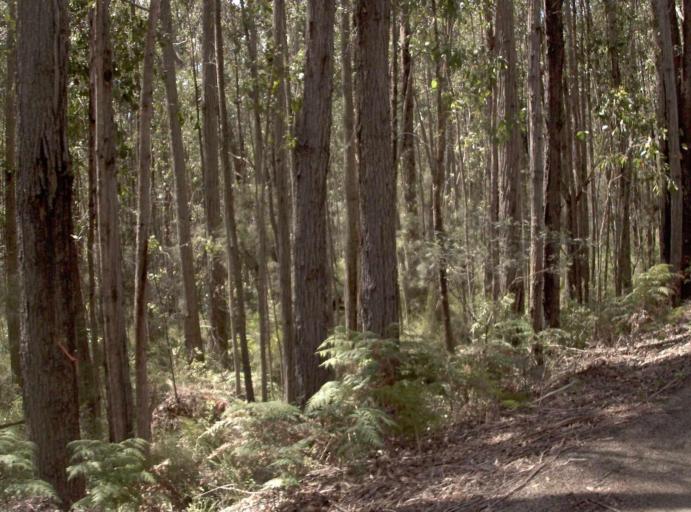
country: AU
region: New South Wales
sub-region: Bombala
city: Bombala
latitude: -37.5706
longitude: 149.3169
